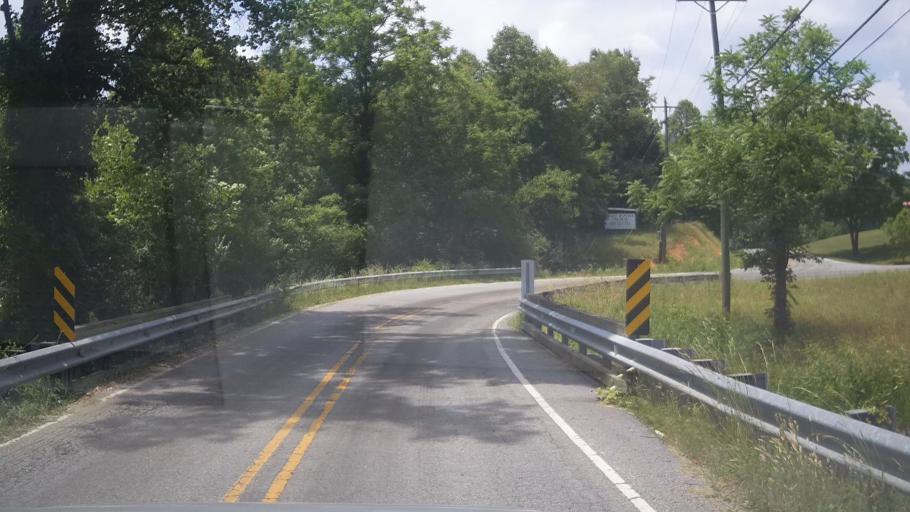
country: US
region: North Carolina
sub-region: McDowell County
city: West Marion
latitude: 35.6395
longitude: -82.0127
